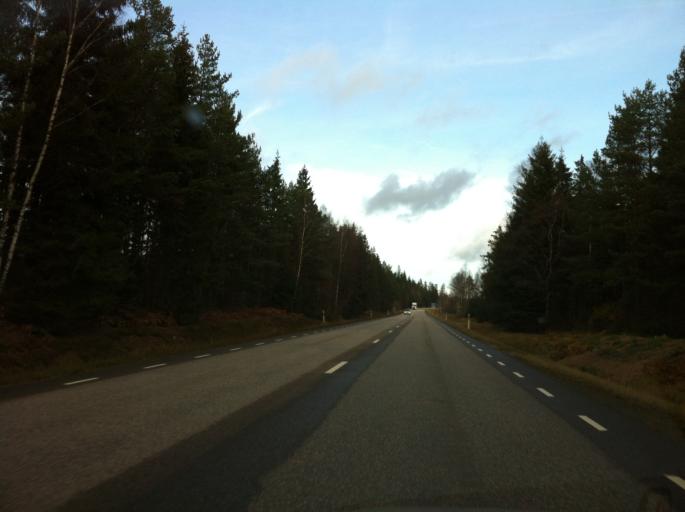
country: SE
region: Kronoberg
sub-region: Almhults Kommun
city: AElmhult
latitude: 56.5607
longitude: 14.1814
